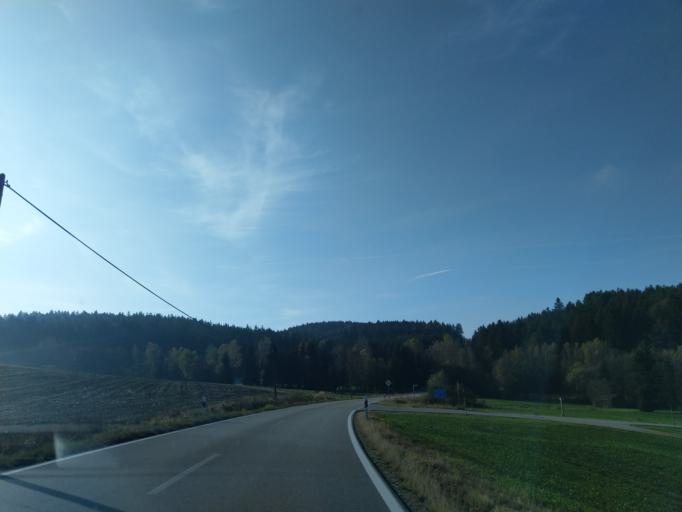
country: DE
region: Bavaria
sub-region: Lower Bavaria
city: Kirchberg
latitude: 48.9011
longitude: 13.1383
